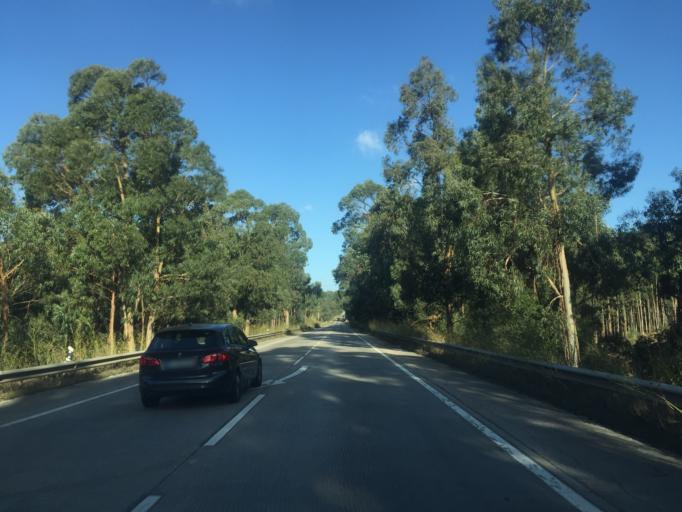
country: PT
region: Santarem
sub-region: Rio Maior
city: Rio Maior
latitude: 39.3328
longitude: -8.9610
